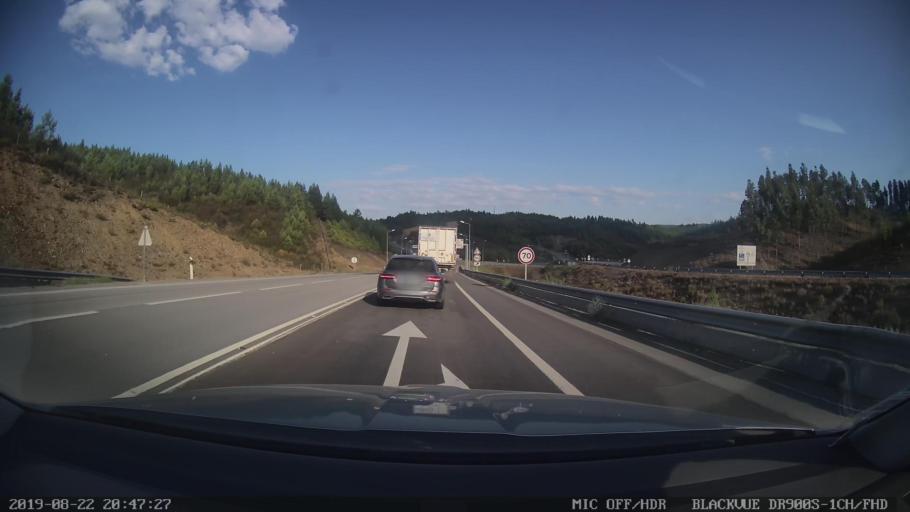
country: PT
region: Castelo Branco
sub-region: Proenca-A-Nova
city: Proenca-a-Nova
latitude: 39.7329
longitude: -7.8896
